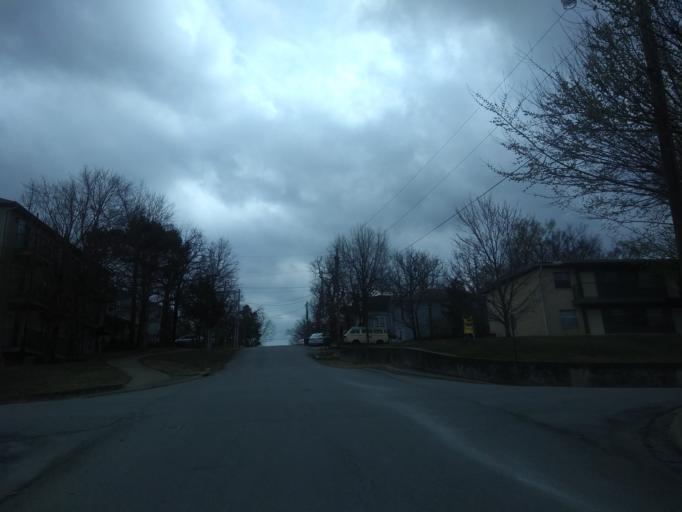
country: US
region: Arkansas
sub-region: Washington County
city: Fayetteville
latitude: 36.0761
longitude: -94.1742
